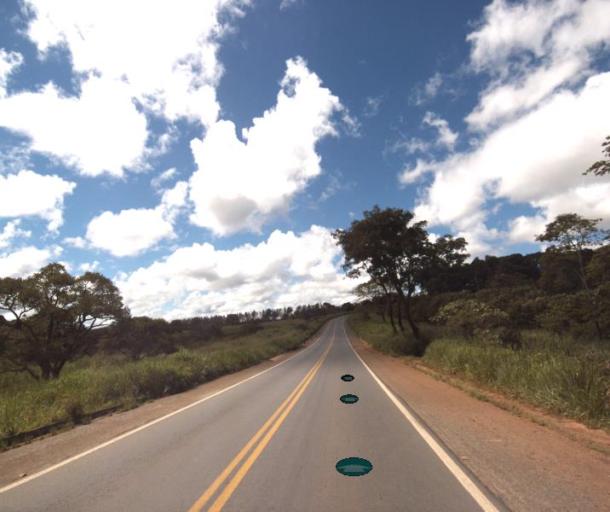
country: BR
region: Goias
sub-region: Petrolina De Goias
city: Petrolina de Goias
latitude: -15.9312
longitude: -49.2067
